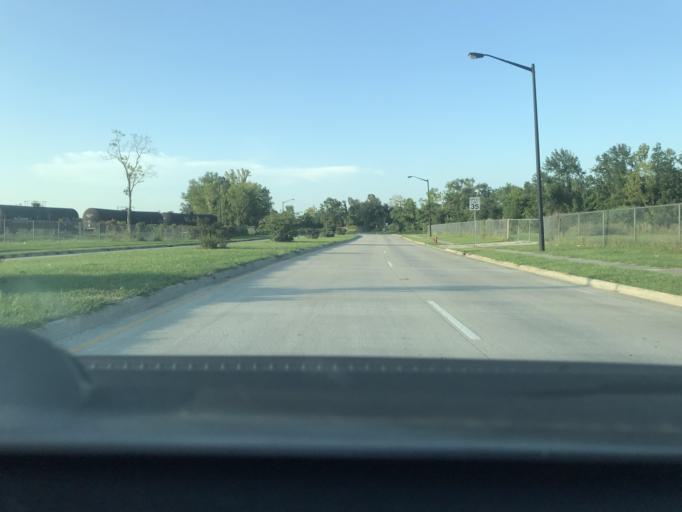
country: US
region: Louisiana
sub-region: Calcasieu Parish
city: Lake Charles
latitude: 30.2451
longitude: -93.2040
